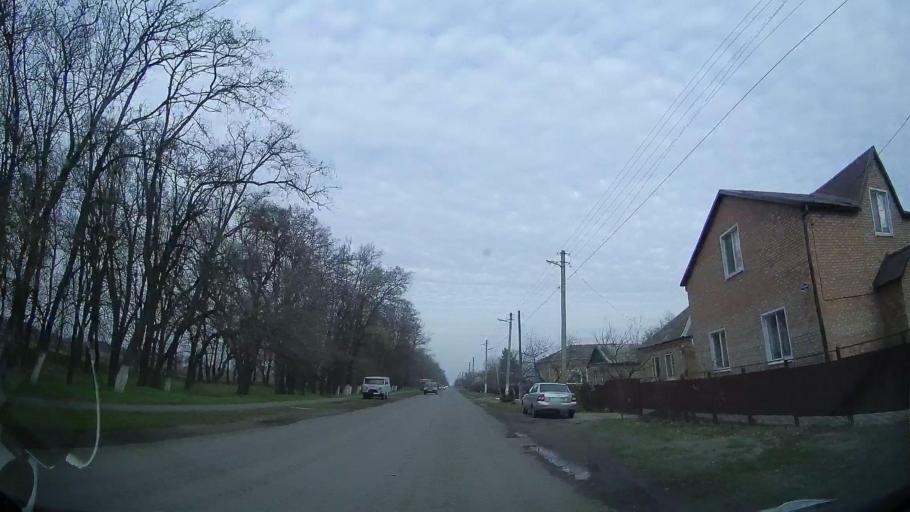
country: RU
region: Rostov
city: Zernograd
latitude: 46.8602
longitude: 40.3221
